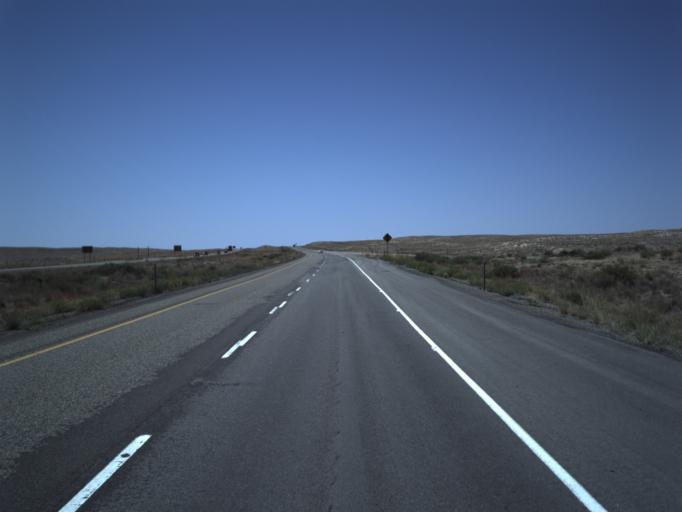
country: US
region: Colorado
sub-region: Mesa County
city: Loma
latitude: 39.1129
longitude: -109.1853
